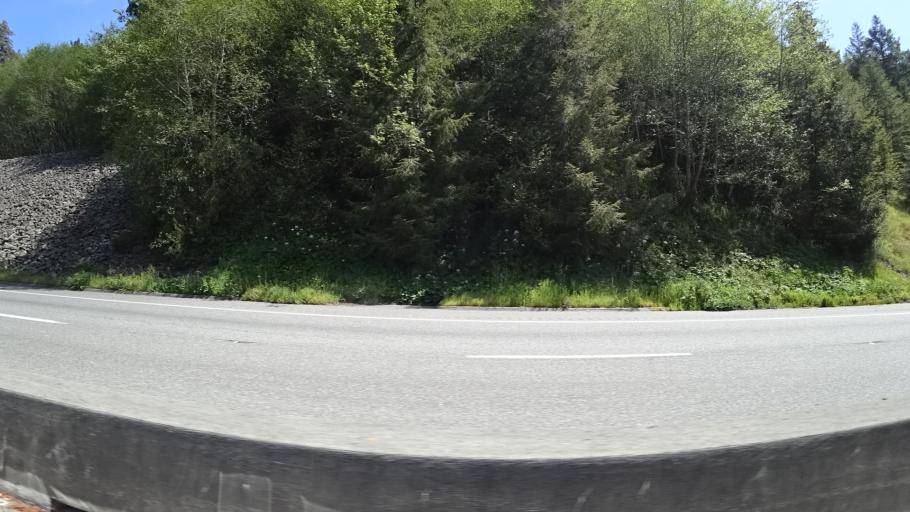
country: US
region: California
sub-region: Humboldt County
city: Westhaven-Moonstone
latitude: 41.3735
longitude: -123.9921
